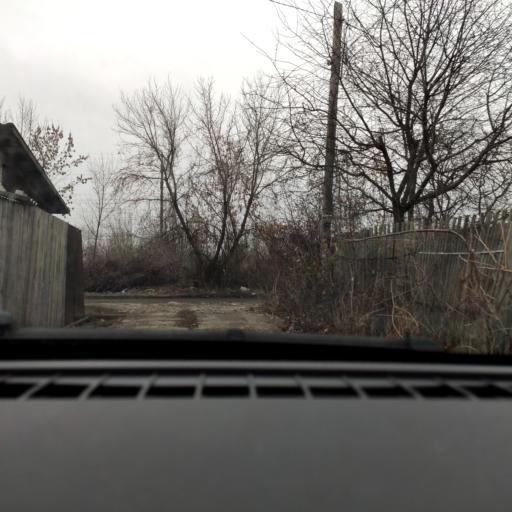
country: RU
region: Voronezj
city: Maslovka
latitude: 51.6114
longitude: 39.2734
